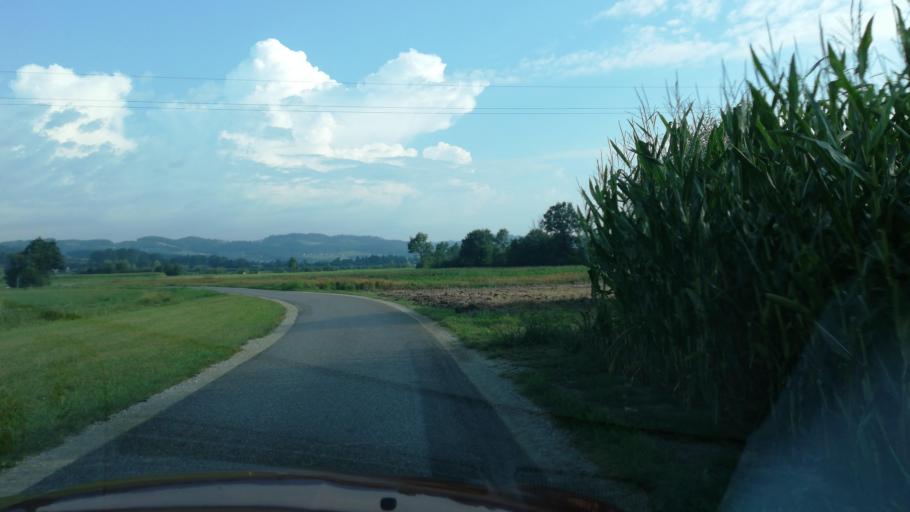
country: AT
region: Upper Austria
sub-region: Politischer Bezirk Urfahr-Umgebung
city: Feldkirchen an der Donau
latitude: 48.3463
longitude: 13.9804
